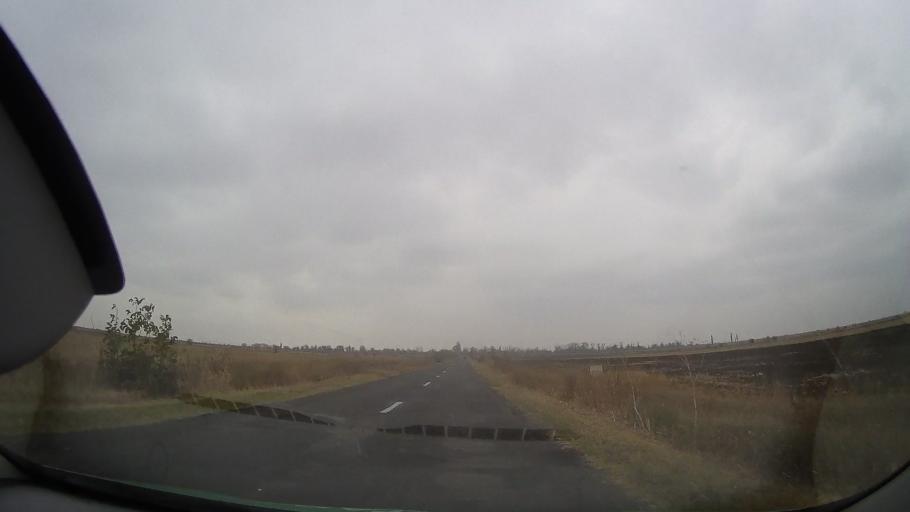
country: RO
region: Ialomita
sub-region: Comuna Garbovi
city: Garbovi
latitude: 44.7657
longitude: 26.7934
